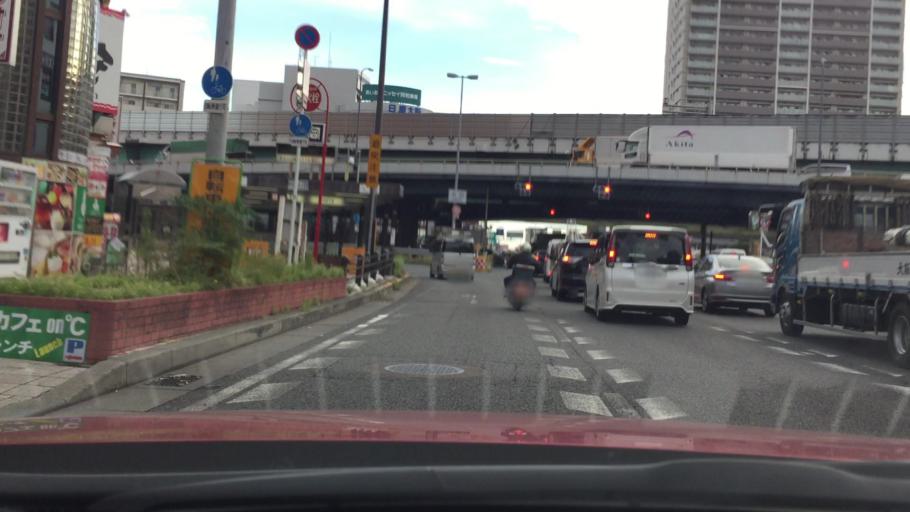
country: JP
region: Osaka
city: Kadoma
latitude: 34.7490
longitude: 135.5775
